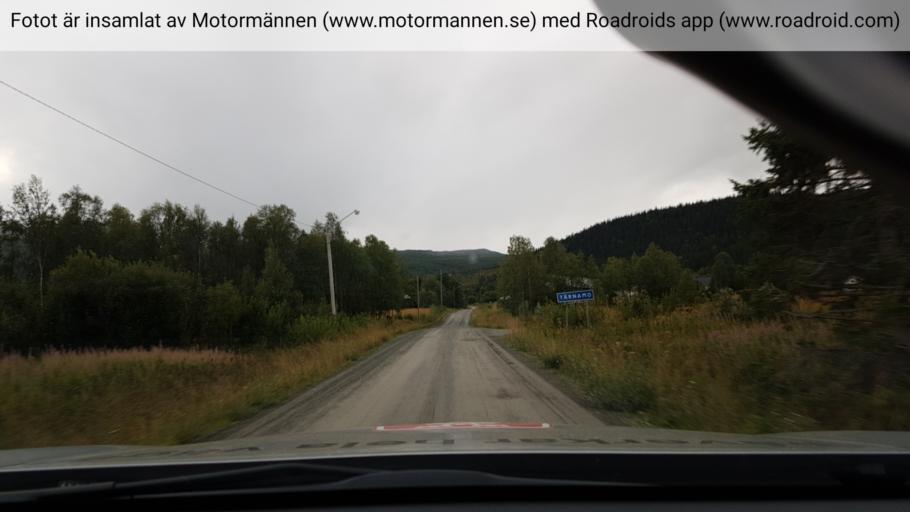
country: NO
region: Nordland
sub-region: Hattfjelldal
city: Hattfjelldal
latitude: 65.6589
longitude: 15.1428
